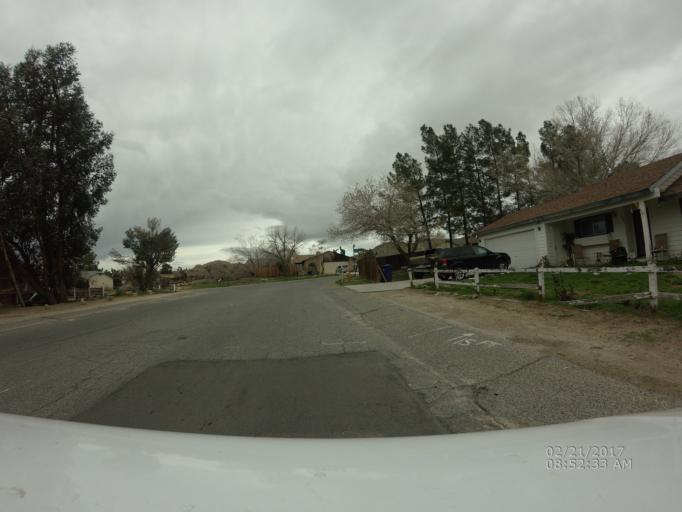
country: US
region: California
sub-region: Los Angeles County
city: Lake Los Angeles
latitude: 34.5980
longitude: -117.8291
